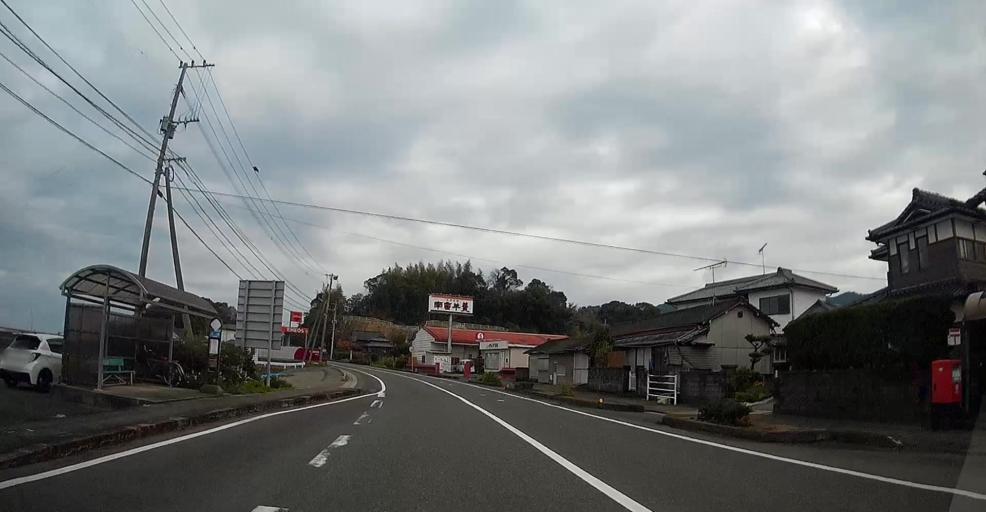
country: JP
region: Kumamoto
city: Hondo
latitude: 32.4610
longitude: 130.2354
